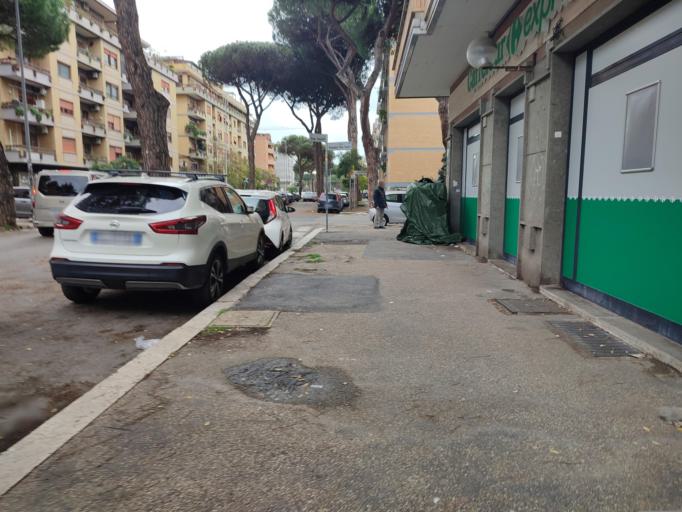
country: IT
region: Latium
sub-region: Citta metropolitana di Roma Capitale
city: Lido di Ostia
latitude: 41.7373
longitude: 12.2889
